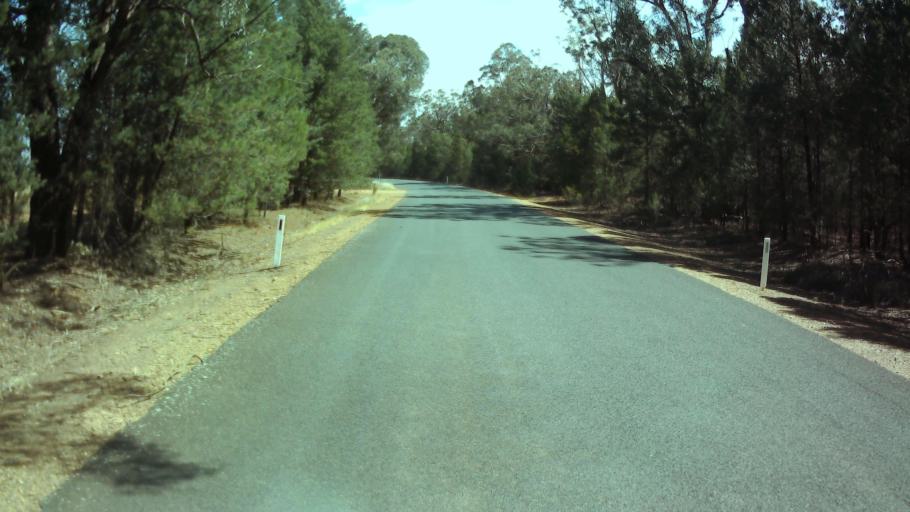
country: AU
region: New South Wales
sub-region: Weddin
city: Grenfell
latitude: -34.0125
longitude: 148.1291
